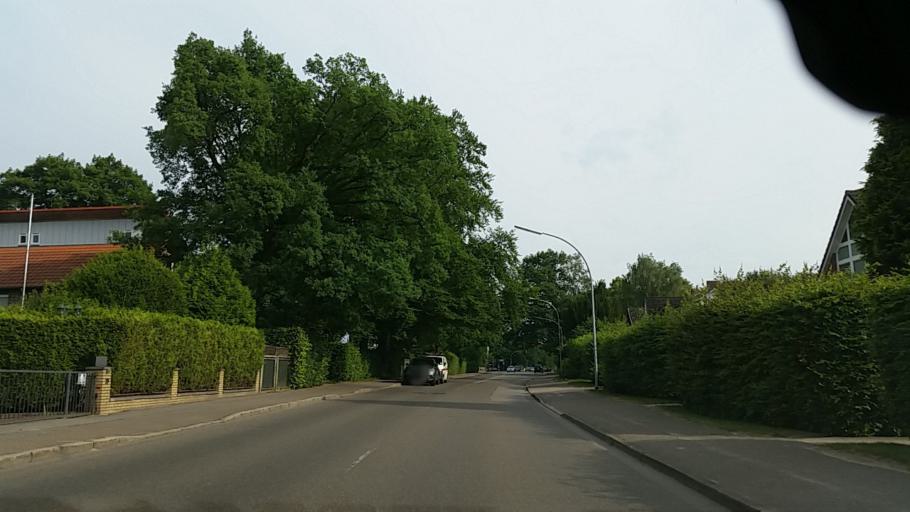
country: DE
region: Schleswig-Holstein
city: Halstenbek
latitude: 53.5932
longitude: 9.8231
